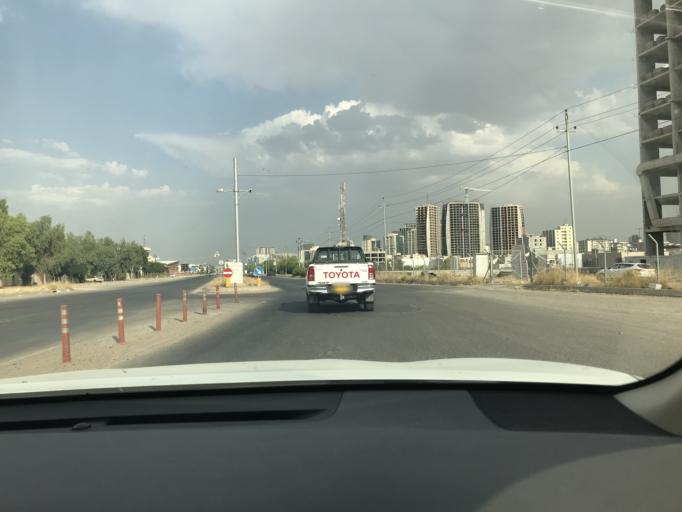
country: IQ
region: Arbil
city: Erbil
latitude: 36.2066
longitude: 43.9606
